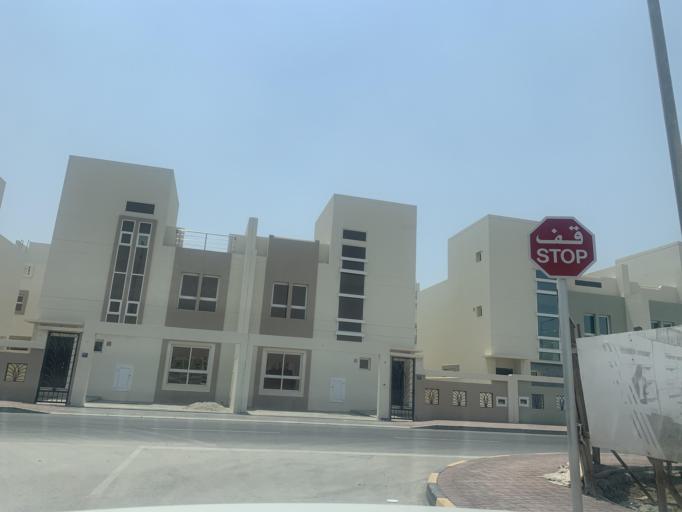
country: BH
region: Central Governorate
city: Madinat Hamad
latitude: 26.1355
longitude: 50.4679
